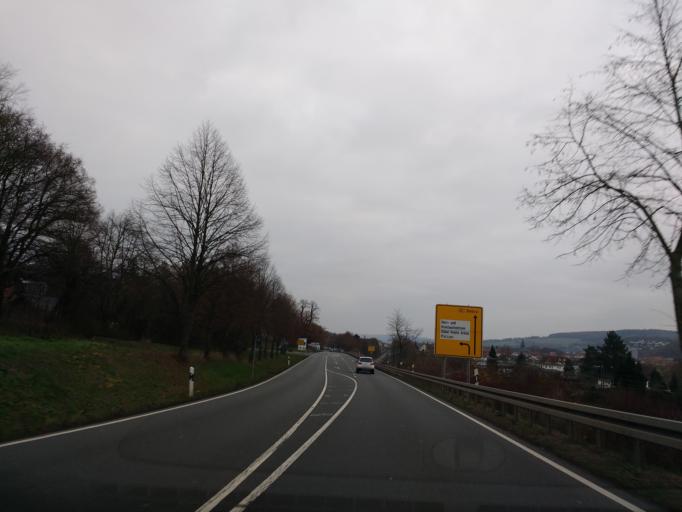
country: DE
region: Hesse
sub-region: Regierungsbezirk Kassel
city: Rotenburg an der Fulda
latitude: 51.0056
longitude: 9.7203
